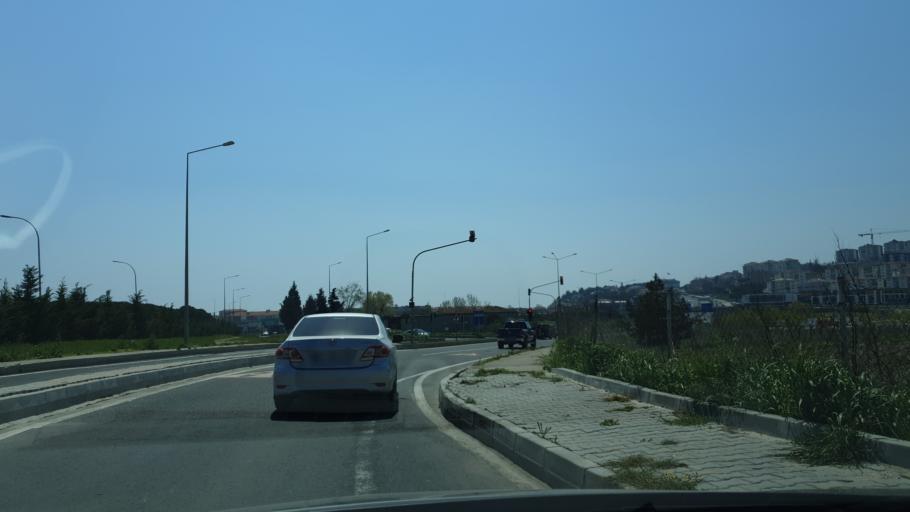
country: TR
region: Tekirdag
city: Tekirdag
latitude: 40.9929
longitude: 27.5770
